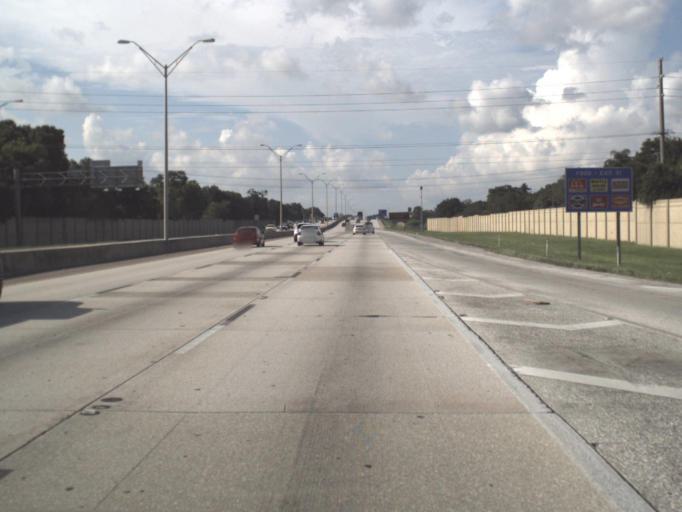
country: US
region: Florida
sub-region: Hillsborough County
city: Lake Magdalene
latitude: 28.0666
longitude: -82.4548
